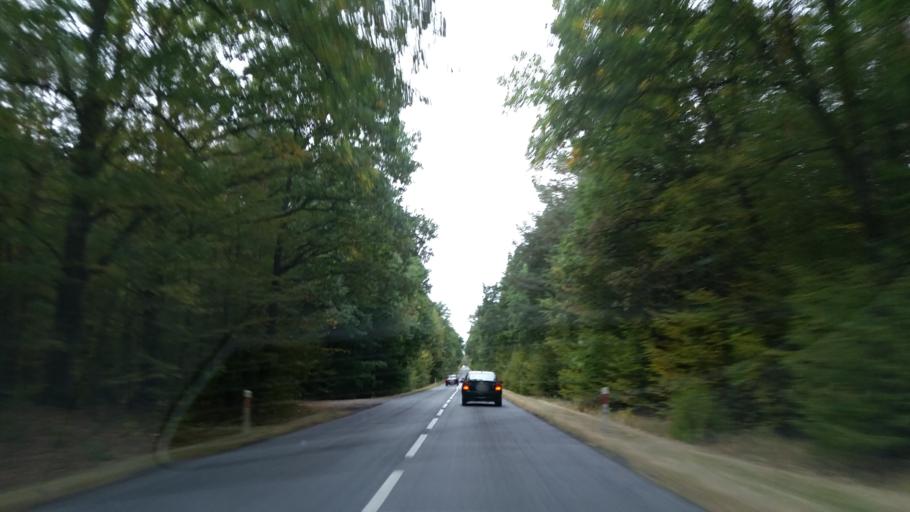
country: PL
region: Lubusz
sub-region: Powiat gorzowski
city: Klodawa
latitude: 52.8150
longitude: 15.2159
